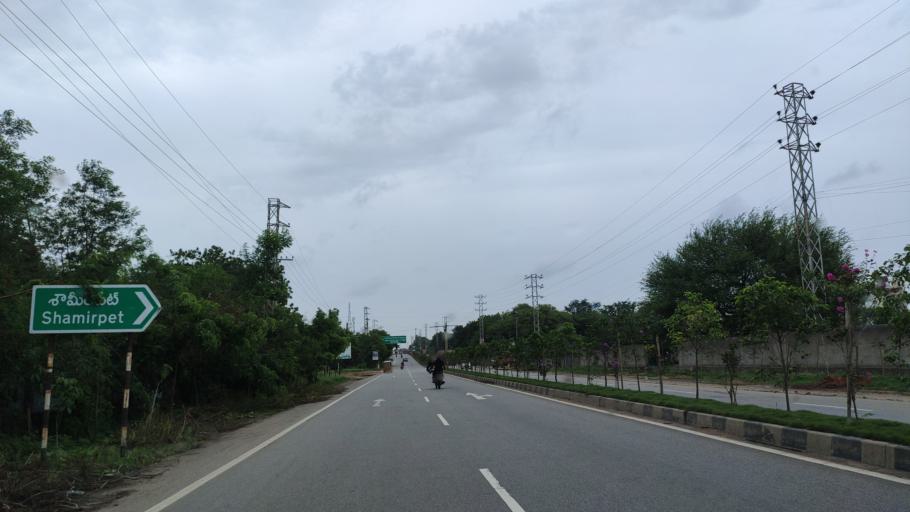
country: IN
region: Telangana
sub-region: Rangareddi
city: Secunderabad
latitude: 17.5859
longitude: 78.5731
